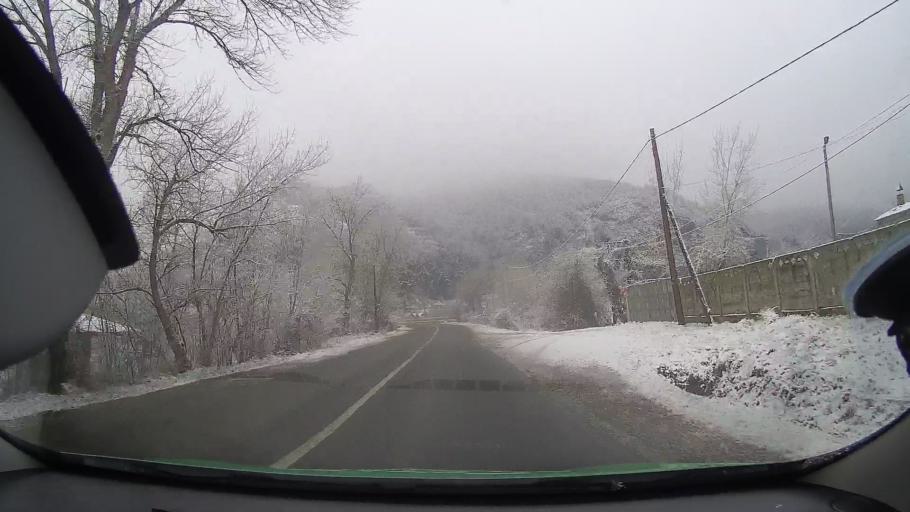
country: RO
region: Cluj
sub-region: Comuna Moldovenesti
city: Moldovenesti
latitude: 46.5111
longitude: 23.6637
